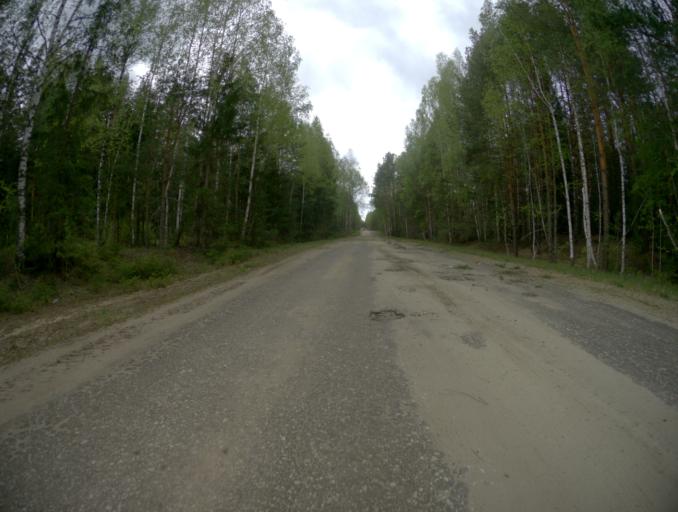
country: RU
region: Vladimir
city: Velikodvorskiy
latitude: 55.2446
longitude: 40.7160
